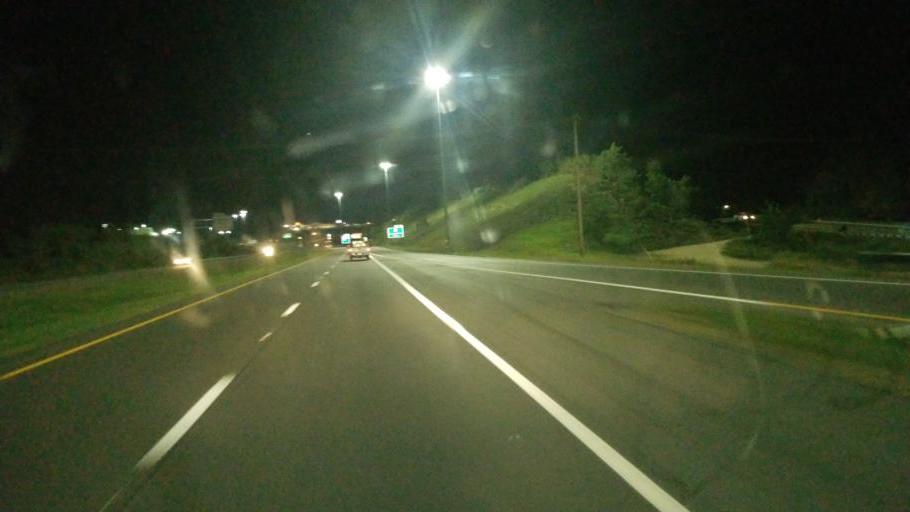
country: US
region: West Virginia
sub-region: Ohio County
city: West Liberty
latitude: 40.0644
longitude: -80.5809
